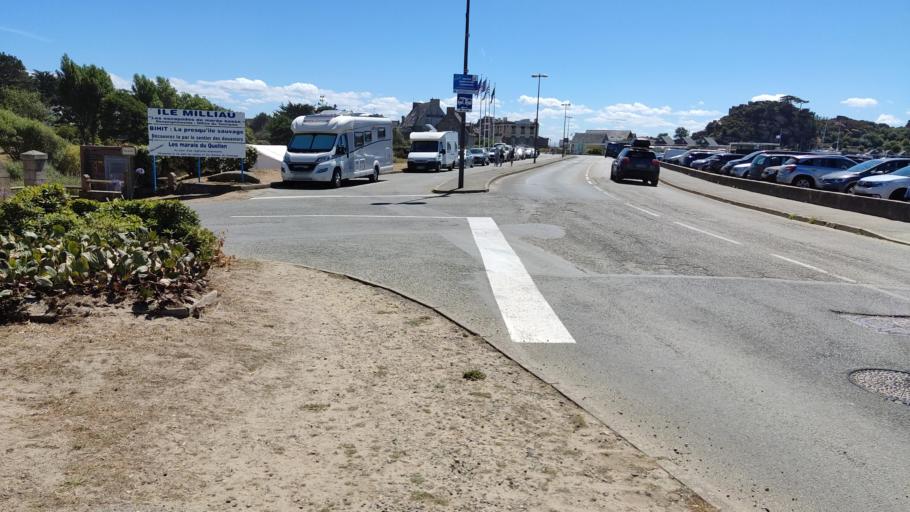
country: FR
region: Brittany
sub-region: Departement des Cotes-d'Armor
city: Trebeurden
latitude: 48.7716
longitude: -3.5833
